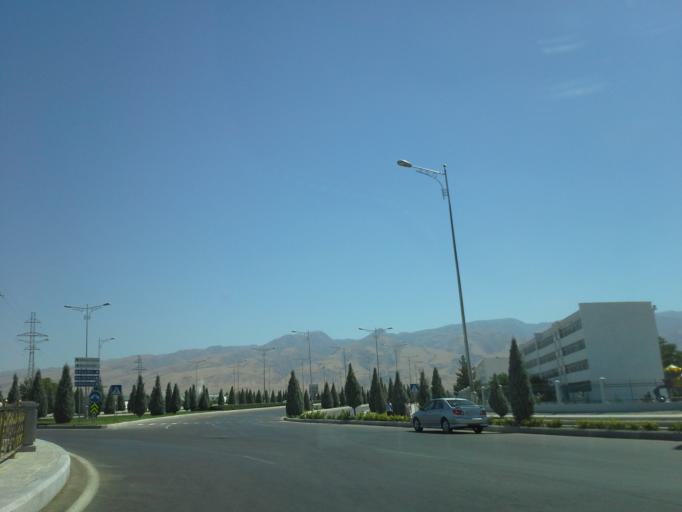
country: TM
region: Ahal
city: Ashgabat
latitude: 37.9311
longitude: 58.2928
